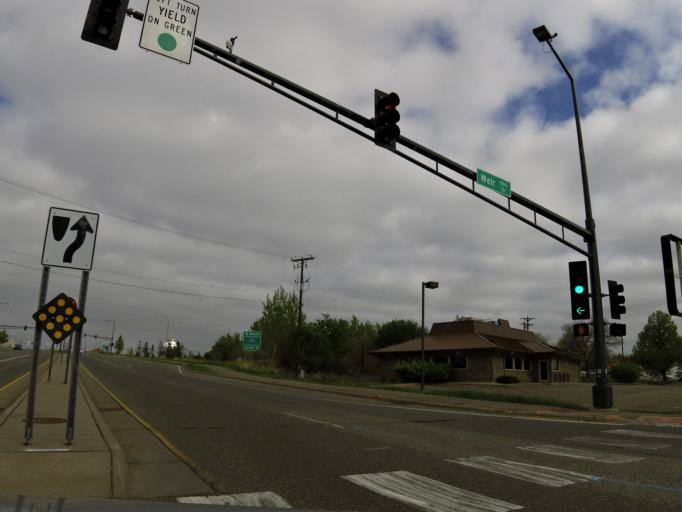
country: US
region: Minnesota
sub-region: Washington County
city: Woodbury
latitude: 44.9265
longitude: -92.9727
